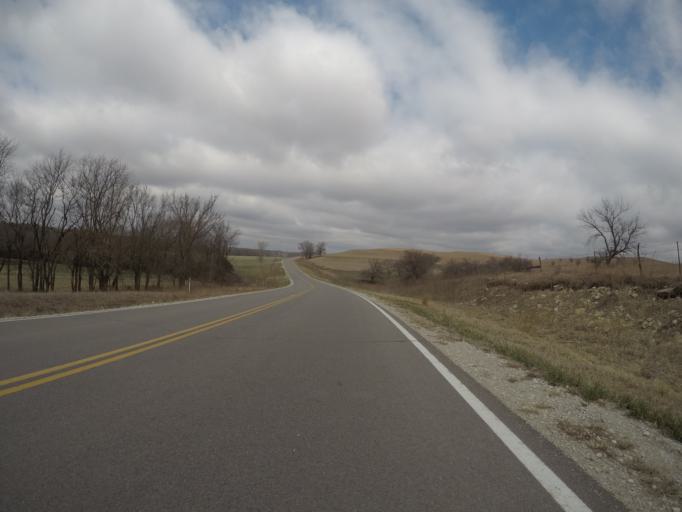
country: US
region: Kansas
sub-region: Pottawatomie County
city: Westmoreland
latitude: 39.4039
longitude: -96.4456
